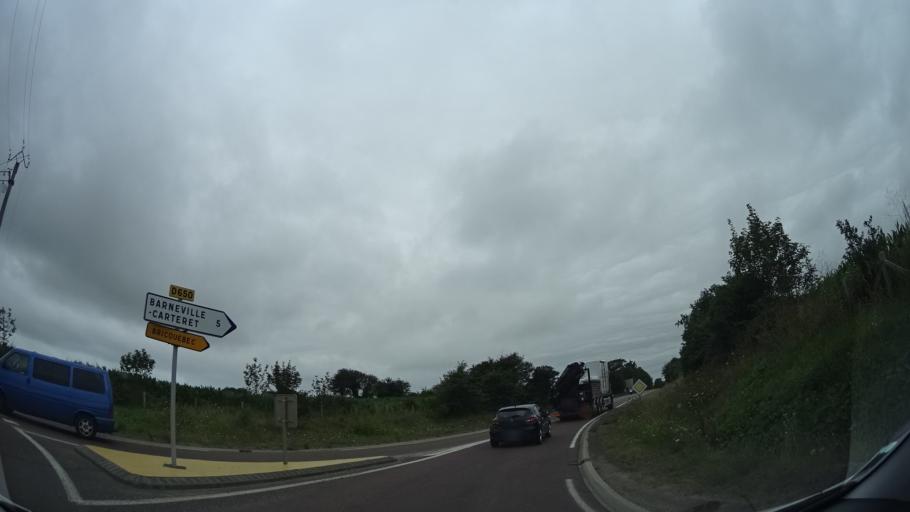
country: FR
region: Lower Normandy
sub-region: Departement de la Manche
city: Portbail
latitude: 49.3617
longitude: -1.6961
